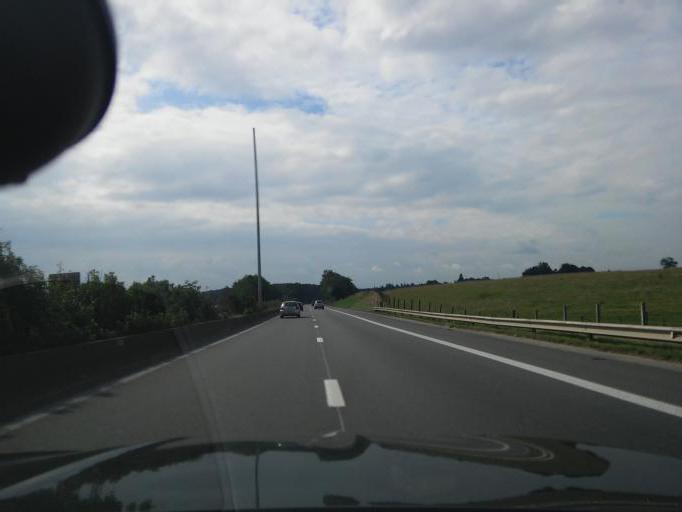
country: BE
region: Wallonia
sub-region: Province du Brabant Wallon
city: Tubize
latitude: 50.7160
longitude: 4.1881
